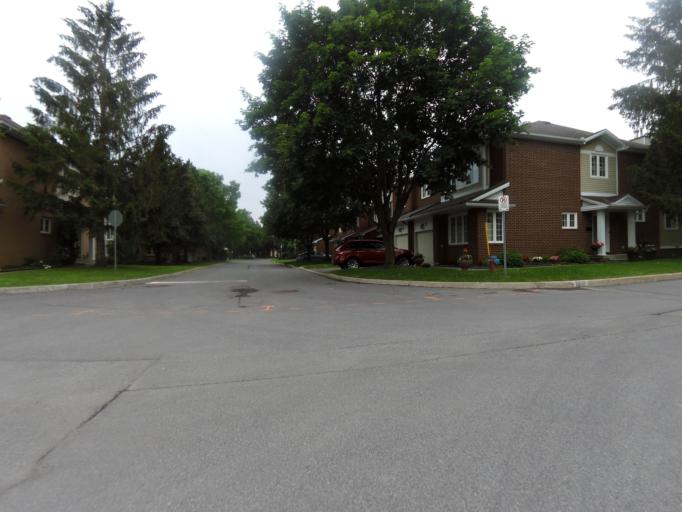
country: CA
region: Ontario
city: Bells Corners
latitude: 45.3404
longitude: -75.7685
